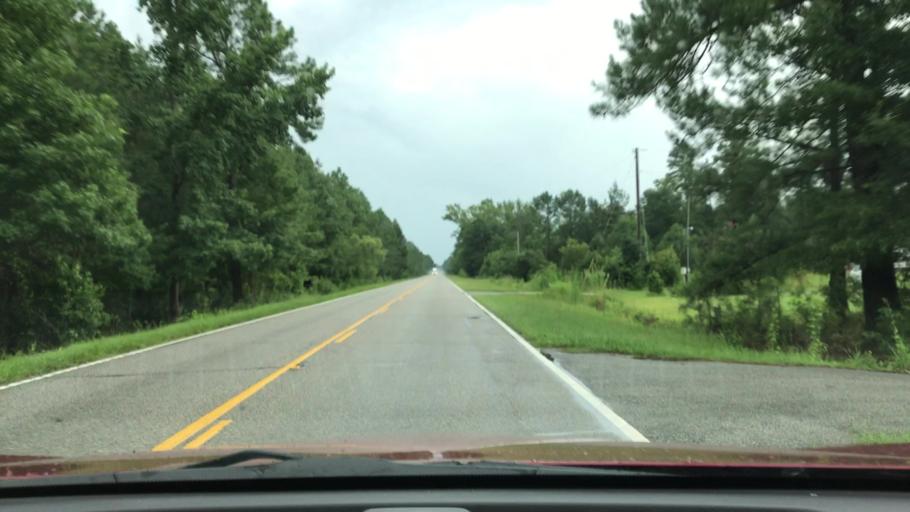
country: US
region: South Carolina
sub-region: Georgetown County
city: Georgetown
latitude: 33.5337
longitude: -79.2354
